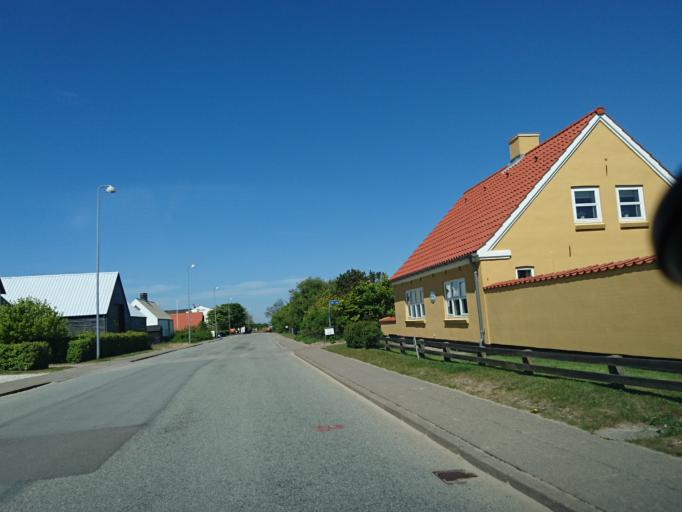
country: DK
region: North Denmark
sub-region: Hjorring Kommune
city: Sindal
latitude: 57.5915
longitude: 10.1860
